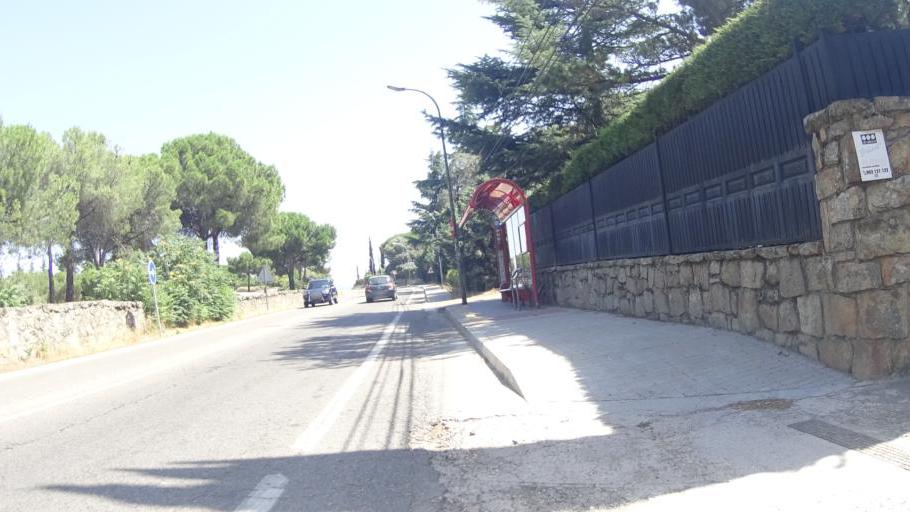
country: ES
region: Madrid
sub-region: Provincia de Madrid
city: Colmenarejo
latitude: 40.5692
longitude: -4.0115
